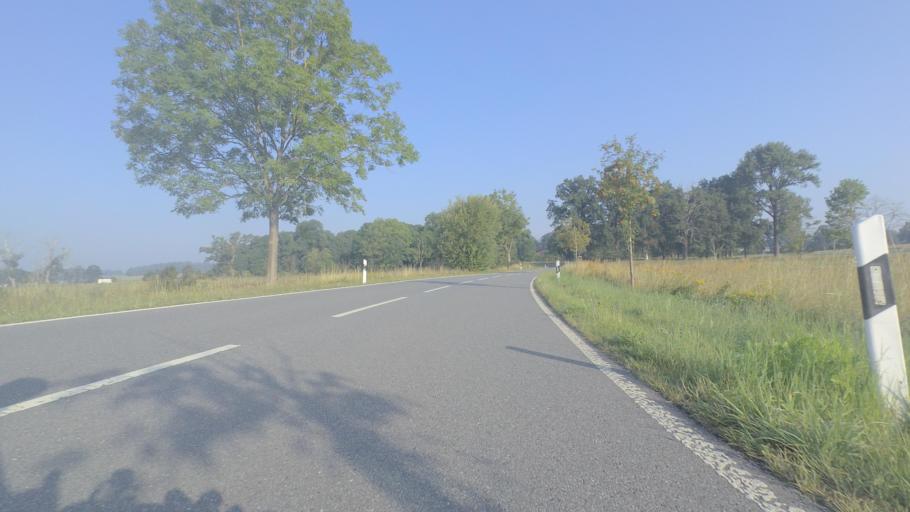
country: DE
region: Brandenburg
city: Heiligengrabe
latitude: 53.2451
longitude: 12.3534
